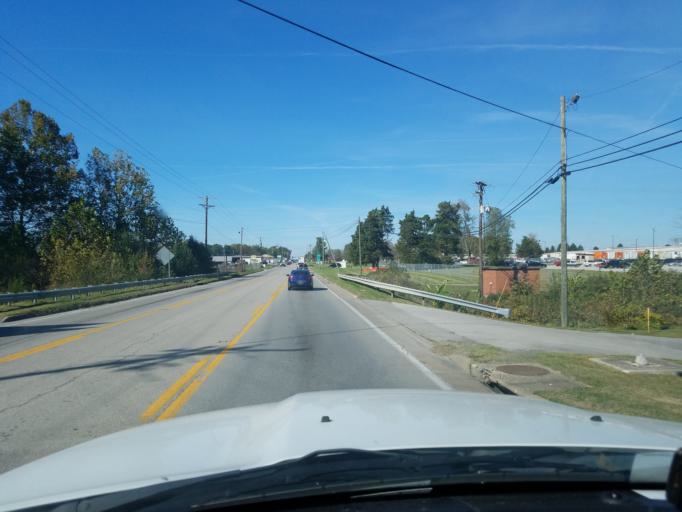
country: US
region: Kentucky
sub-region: Laurel County
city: London
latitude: 37.0901
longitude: -84.0636
